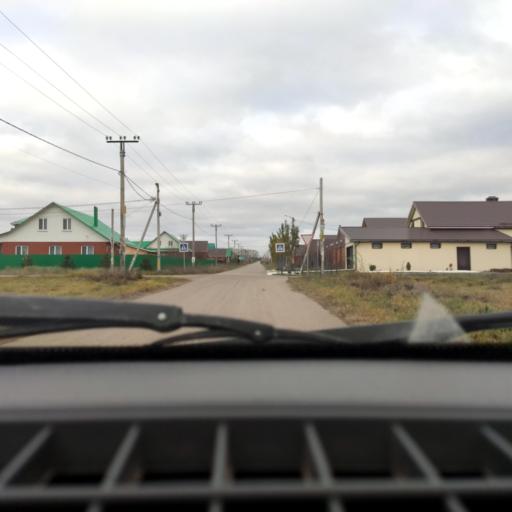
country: RU
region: Bashkortostan
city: Avdon
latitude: 54.6577
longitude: 55.7422
